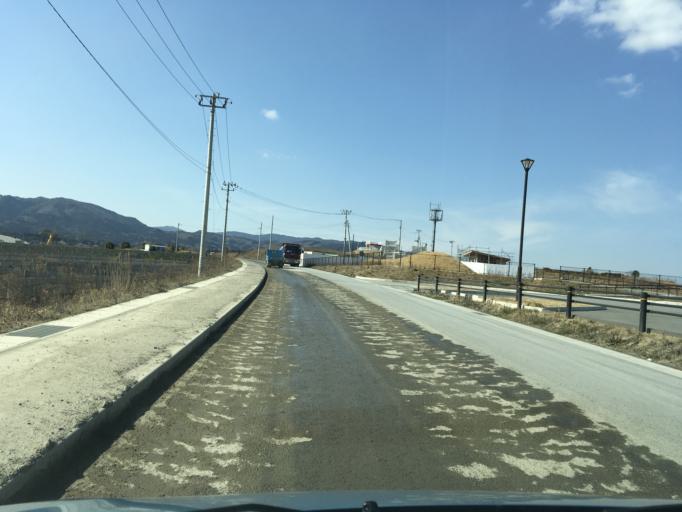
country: JP
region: Iwate
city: Ofunato
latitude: 38.8257
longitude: 141.5890
